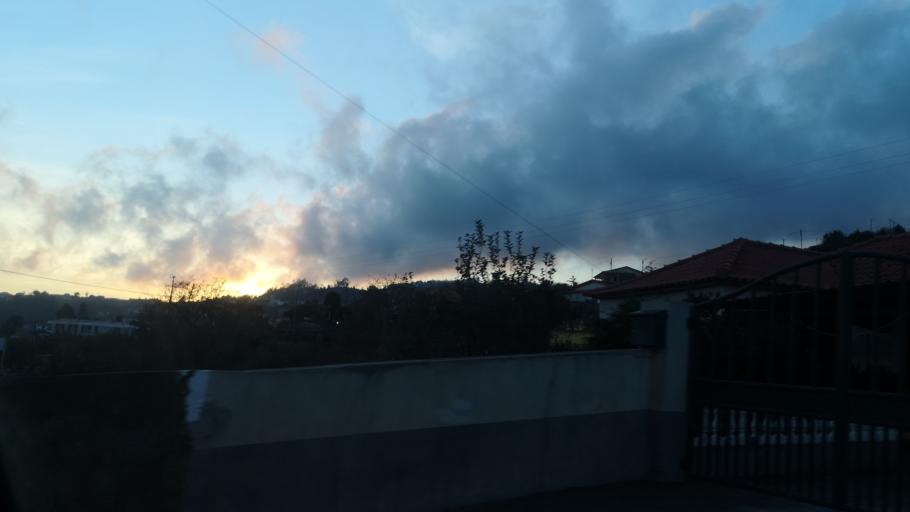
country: PT
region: Madeira
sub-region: Santa Cruz
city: Camacha
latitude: 32.6823
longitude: -16.8274
